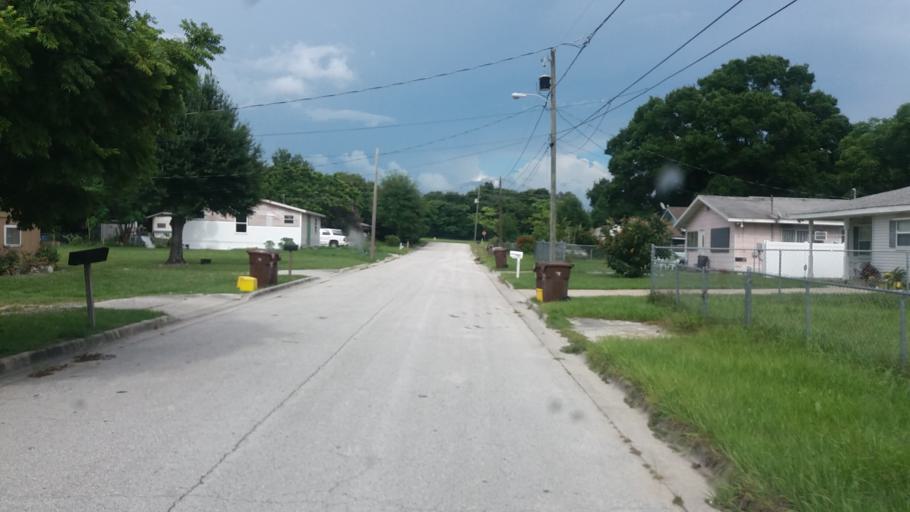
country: US
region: Florida
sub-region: Polk County
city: Lake Wales
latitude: 27.8986
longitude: -81.5951
